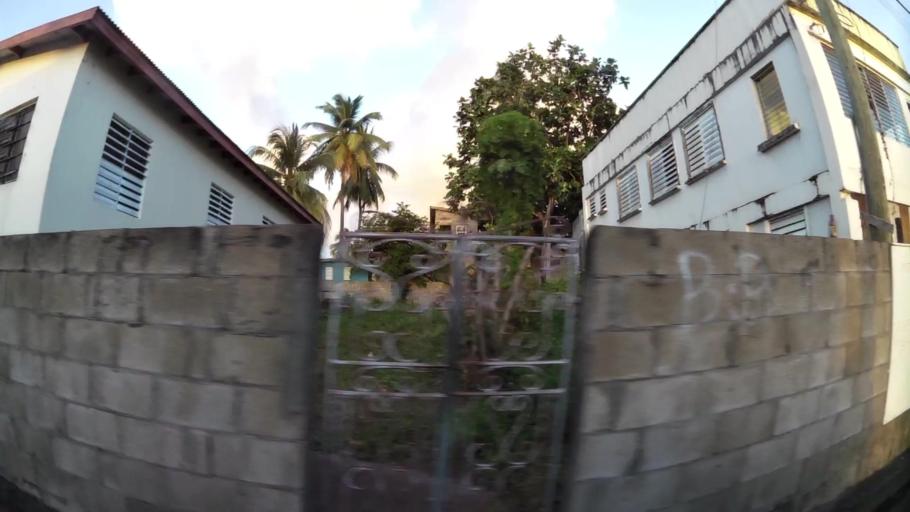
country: KN
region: Saint Anne Sandy Point
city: Sandy Point Town
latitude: 17.3637
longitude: -62.8504
